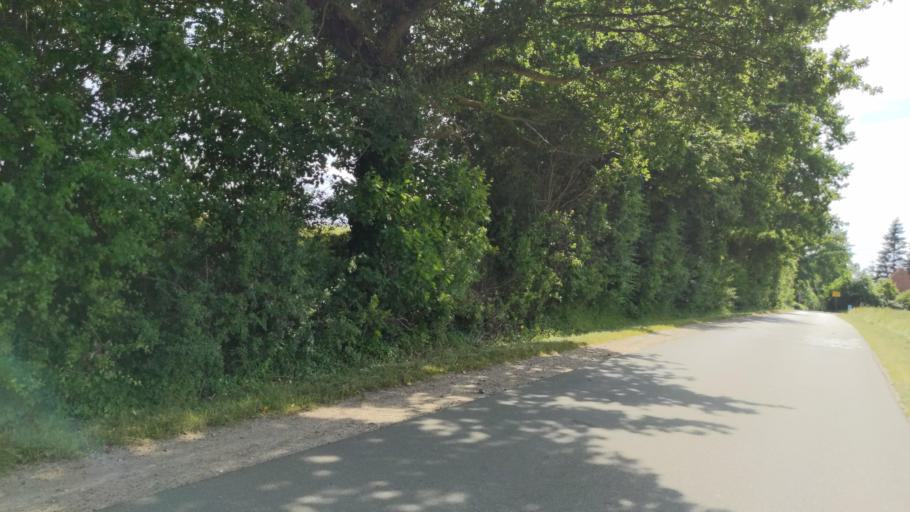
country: DE
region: Mecklenburg-Vorpommern
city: Dassow
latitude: 53.9705
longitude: 10.9677
